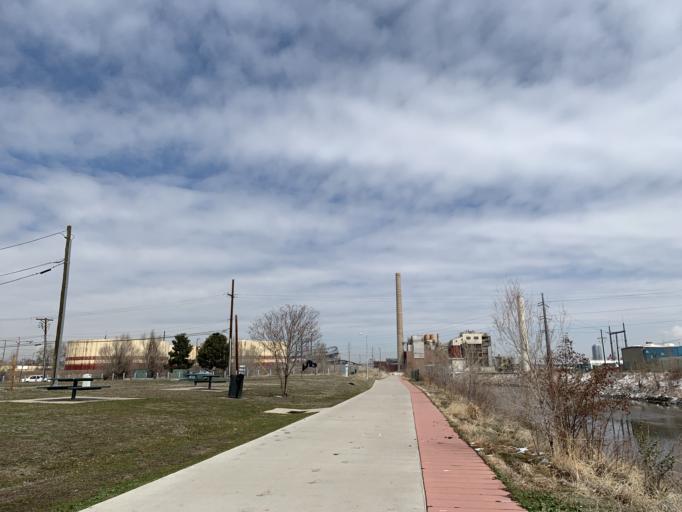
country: US
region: Colorado
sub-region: Denver County
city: Denver
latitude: 39.7332
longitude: -105.0174
